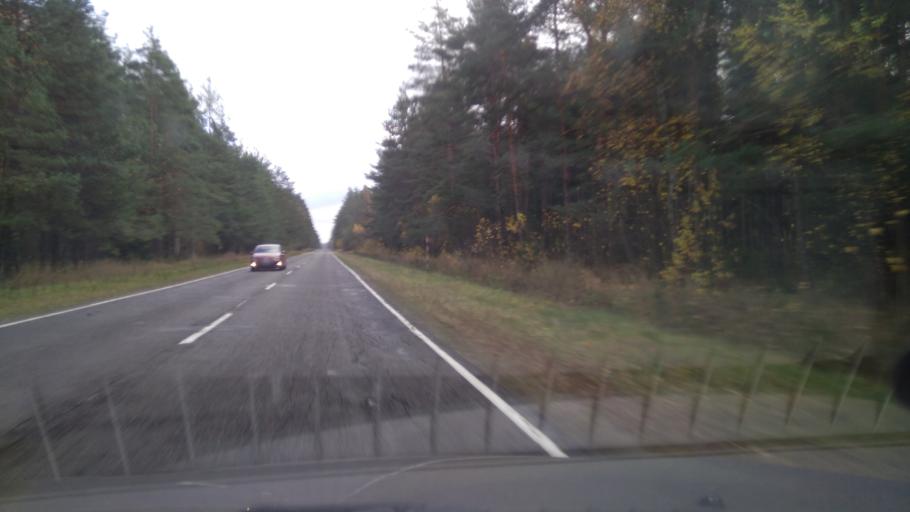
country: BY
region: Minsk
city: Slutsk
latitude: 53.2301
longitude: 27.6889
